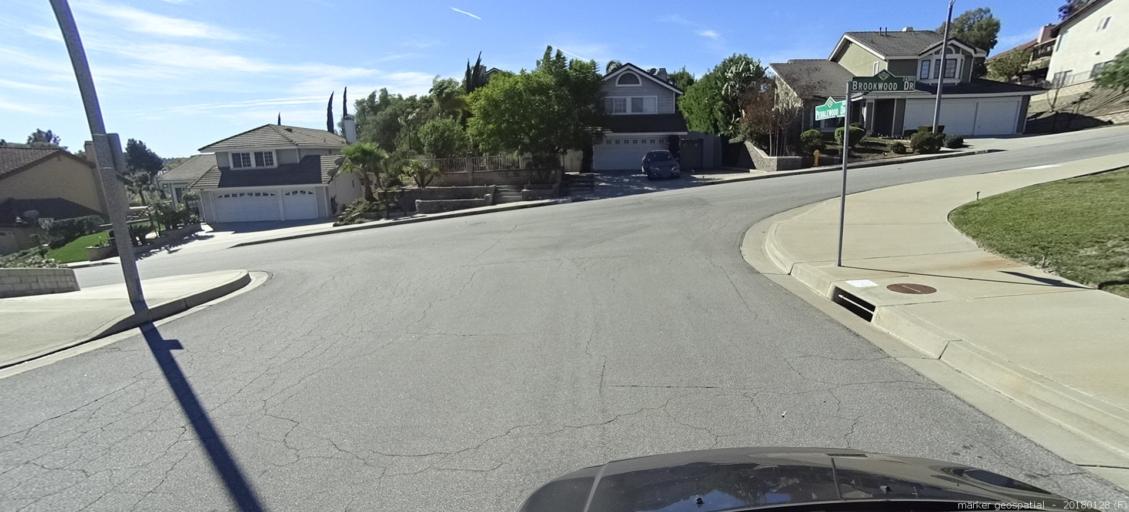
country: US
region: California
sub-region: San Bernardino County
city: Chino Hills
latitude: 33.9994
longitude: -117.7914
